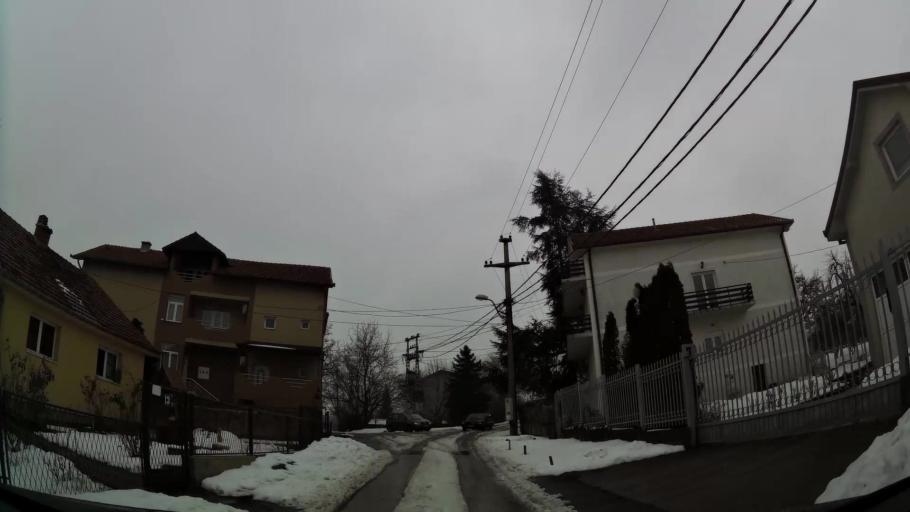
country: RS
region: Central Serbia
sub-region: Belgrade
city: Zvezdara
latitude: 44.7625
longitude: 20.5193
